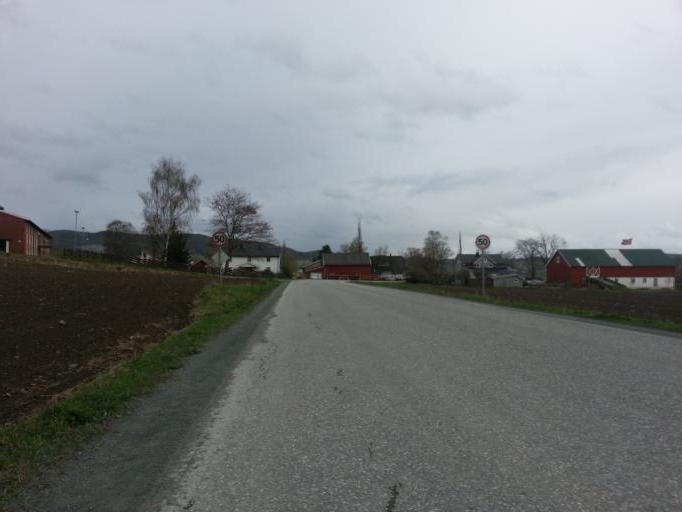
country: NO
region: Nord-Trondelag
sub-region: Levanger
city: Skogn
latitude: 63.6968
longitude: 11.1984
